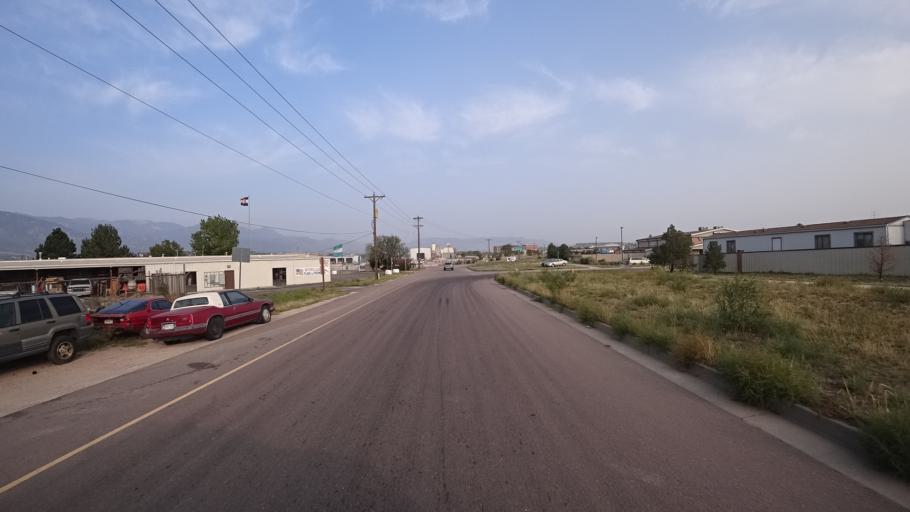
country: US
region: Colorado
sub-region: El Paso County
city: Stratmoor
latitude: 38.7777
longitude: -104.7715
